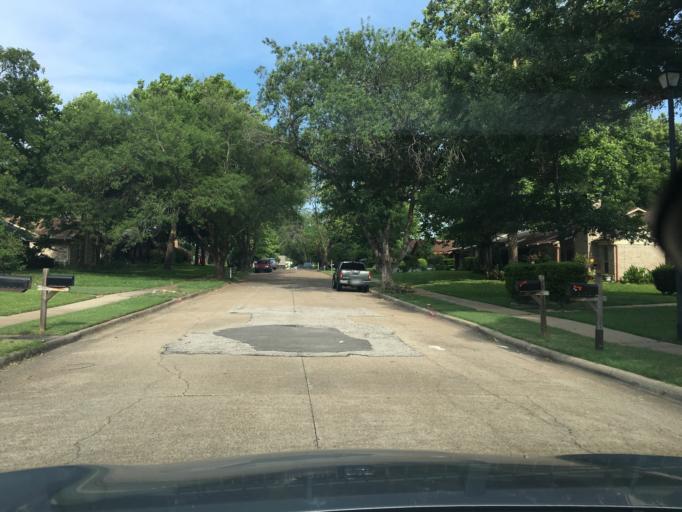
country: US
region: Texas
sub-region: Collin County
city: Plano
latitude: 32.9665
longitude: -96.6710
